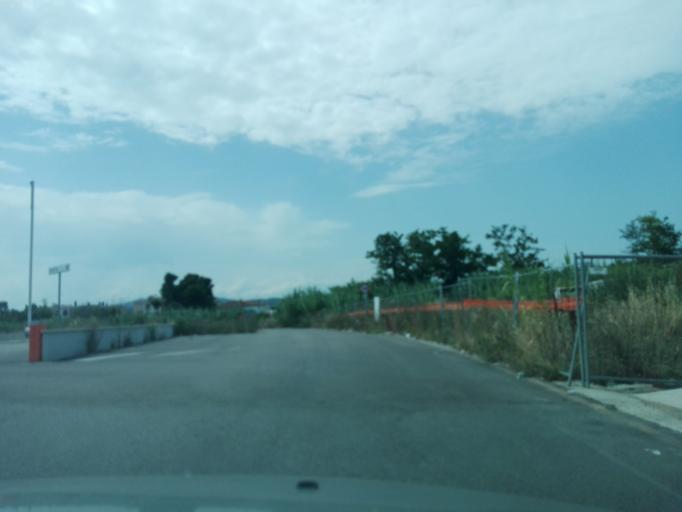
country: IT
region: Abruzzo
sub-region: Provincia di Pescara
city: Montesilvano Marina
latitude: 42.4955
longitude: 14.1259
